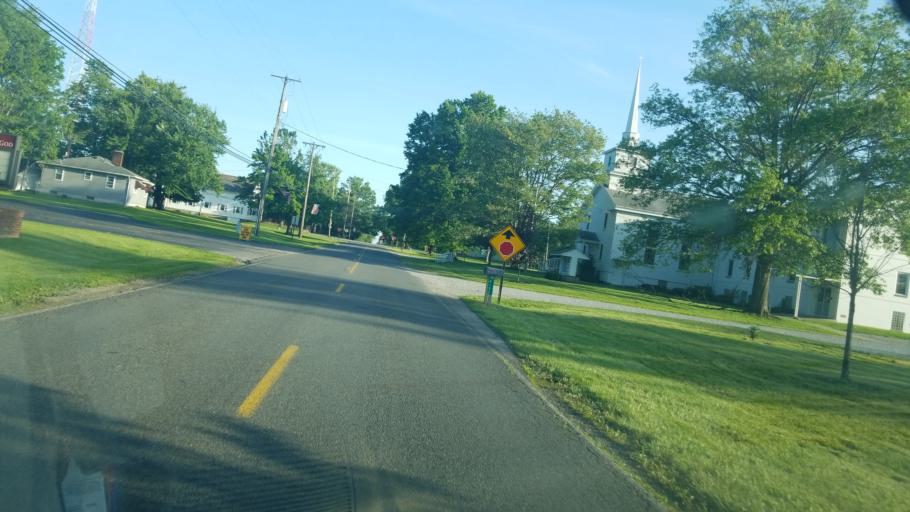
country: US
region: Ohio
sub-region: Portage County
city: Ravenna
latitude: 41.1011
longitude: -81.1459
